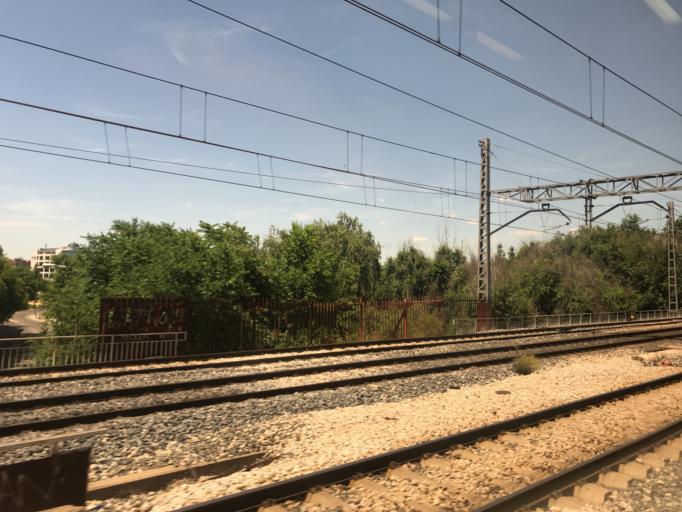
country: ES
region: Madrid
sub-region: Provincia de Madrid
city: Villaverde
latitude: 40.3592
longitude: -3.6815
